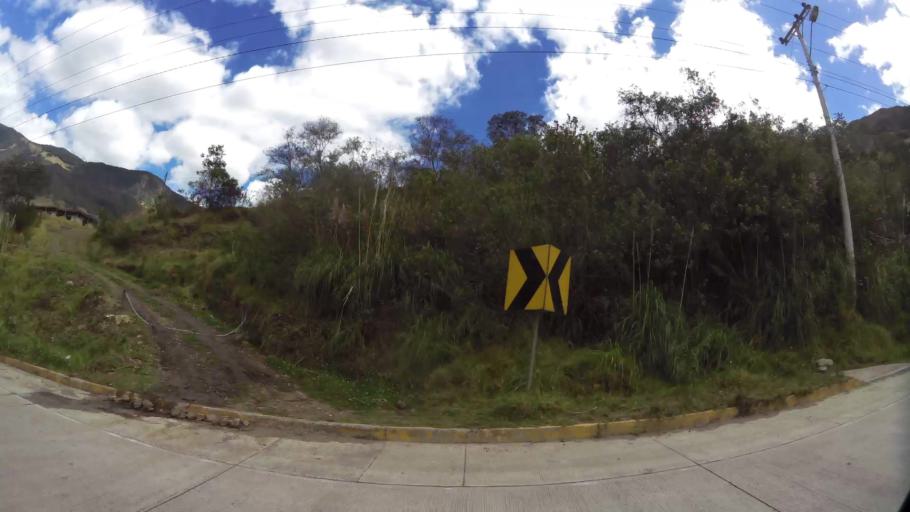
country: EC
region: Azuay
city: Cuenca
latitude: -3.1340
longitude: -79.1210
